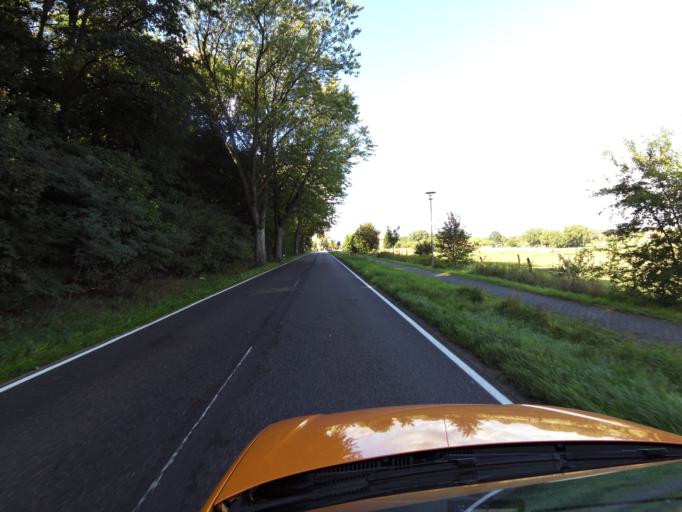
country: DE
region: Brandenburg
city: Michendorf
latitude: 52.3126
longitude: 13.0741
